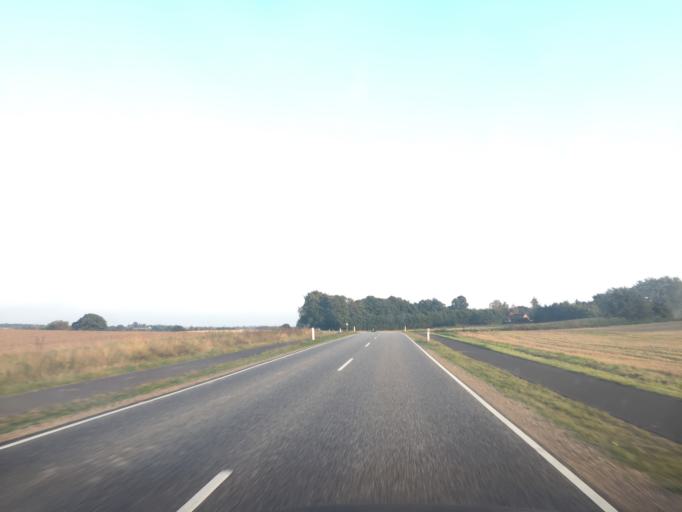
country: DK
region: Zealand
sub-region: Lejre Kommune
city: Kirke Hvalso
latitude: 55.5857
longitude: 11.8826
